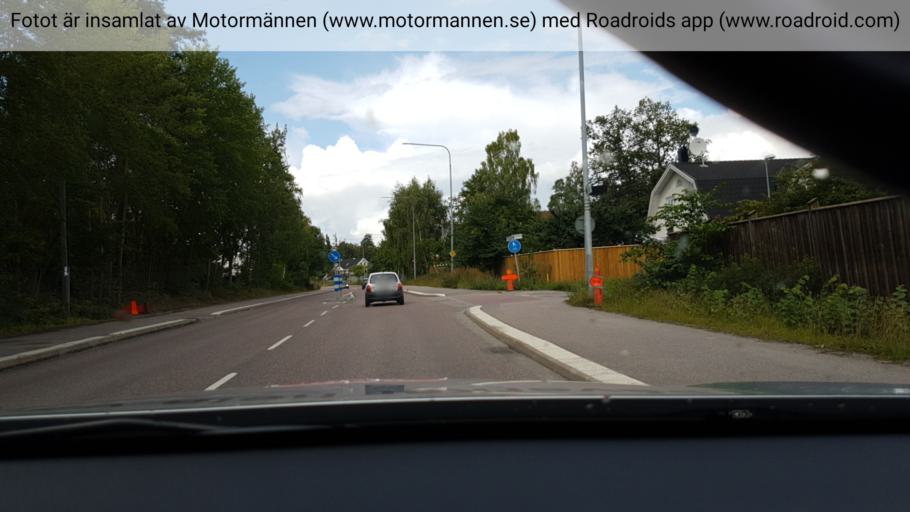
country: SE
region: Stockholm
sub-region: Huddinge Kommun
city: Huddinge
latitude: 59.2575
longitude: 17.9796
